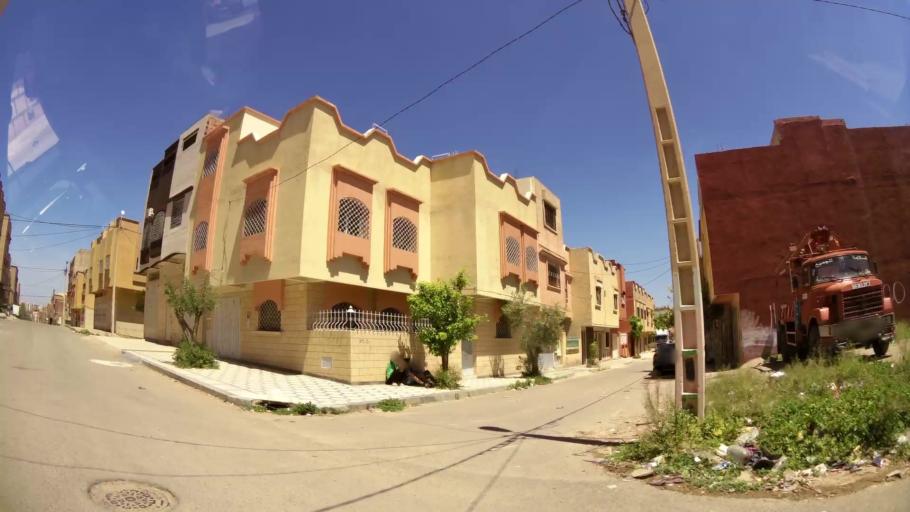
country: MA
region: Oriental
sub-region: Oujda-Angad
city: Oujda
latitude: 34.6568
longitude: -1.9264
